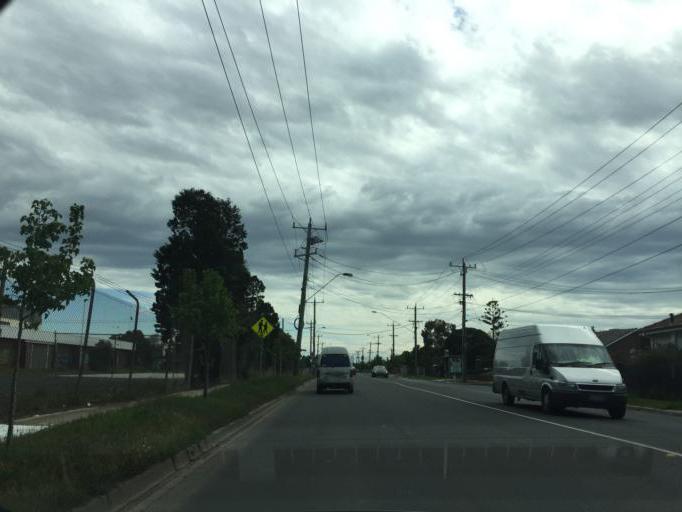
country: AU
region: Victoria
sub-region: Maribyrnong
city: Braybrook
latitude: -37.7899
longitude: 144.8638
